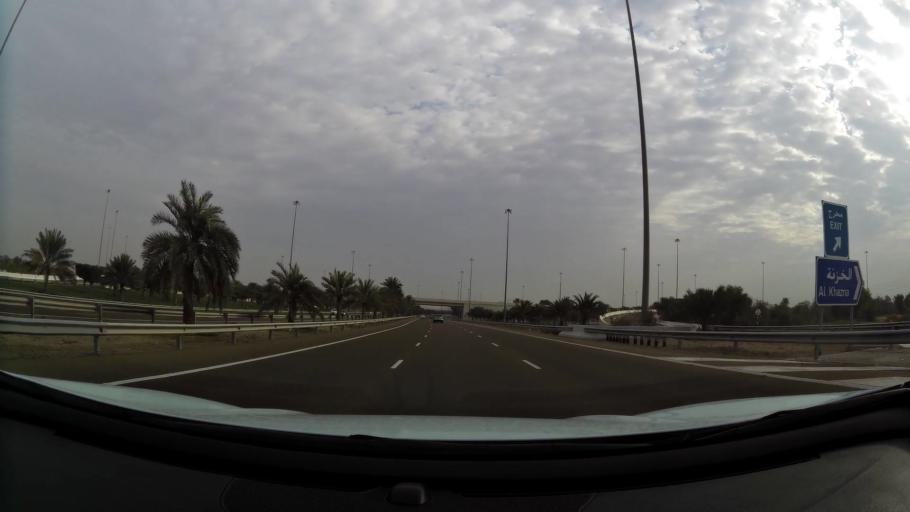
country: AE
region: Abu Dhabi
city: Al Ain
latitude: 24.1743
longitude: 55.1338
